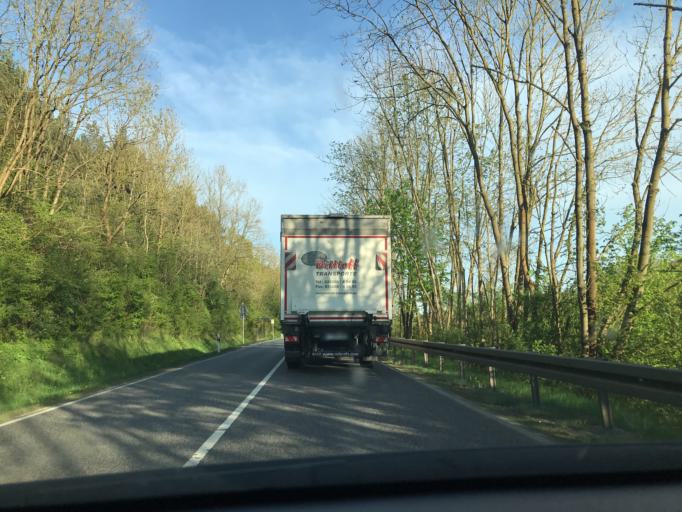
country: DE
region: Thuringia
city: Geisleden
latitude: 51.3584
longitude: 10.1776
